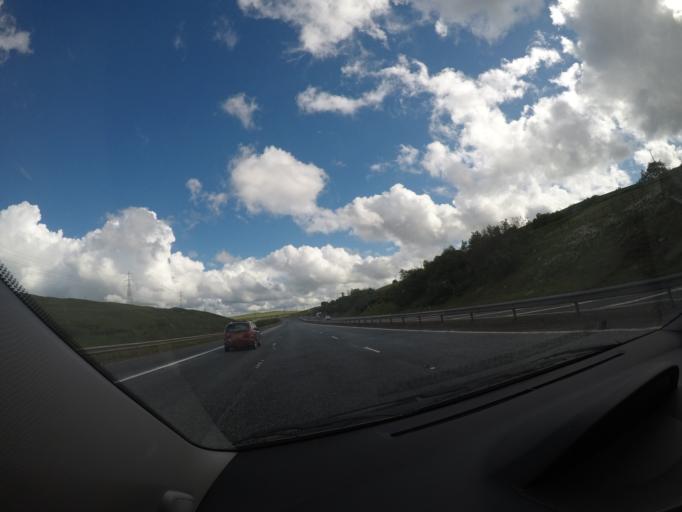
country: GB
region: Scotland
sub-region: South Lanarkshire
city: Douglas
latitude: 55.5547
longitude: -3.8014
